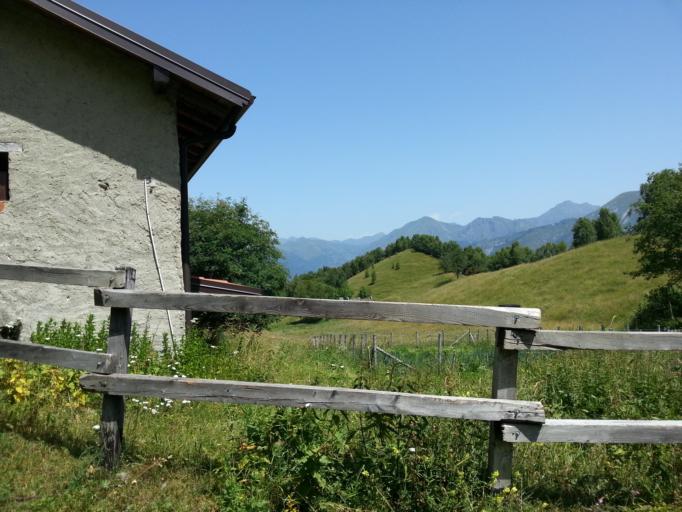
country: IT
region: Lombardy
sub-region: Provincia di Lecco
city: Cremeno
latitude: 45.9122
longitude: 9.4521
